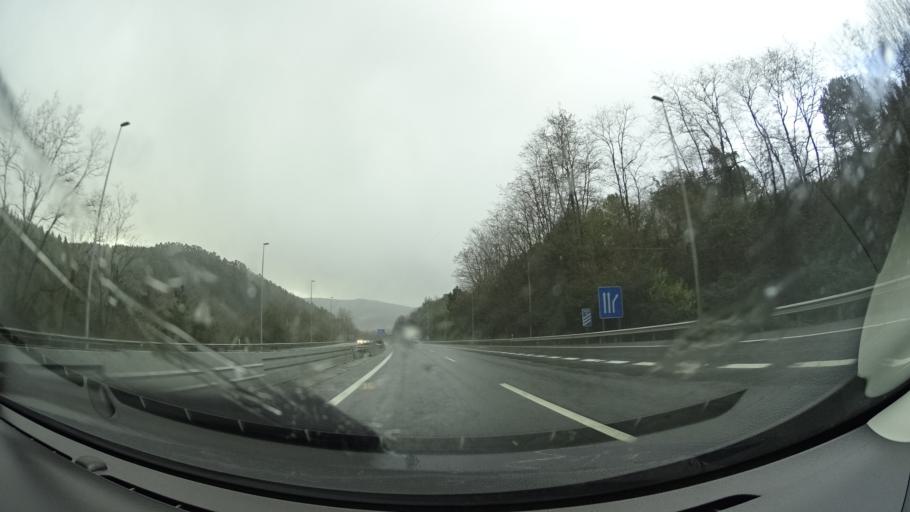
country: ES
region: Basque Country
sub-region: Bizkaia
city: Derio
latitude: 43.3140
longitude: -2.8783
